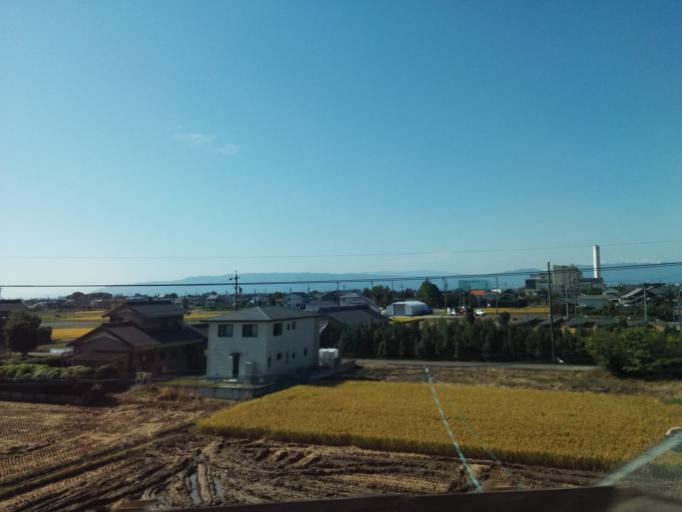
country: JP
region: Aichi
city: Inazawa
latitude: 35.2524
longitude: 136.7671
